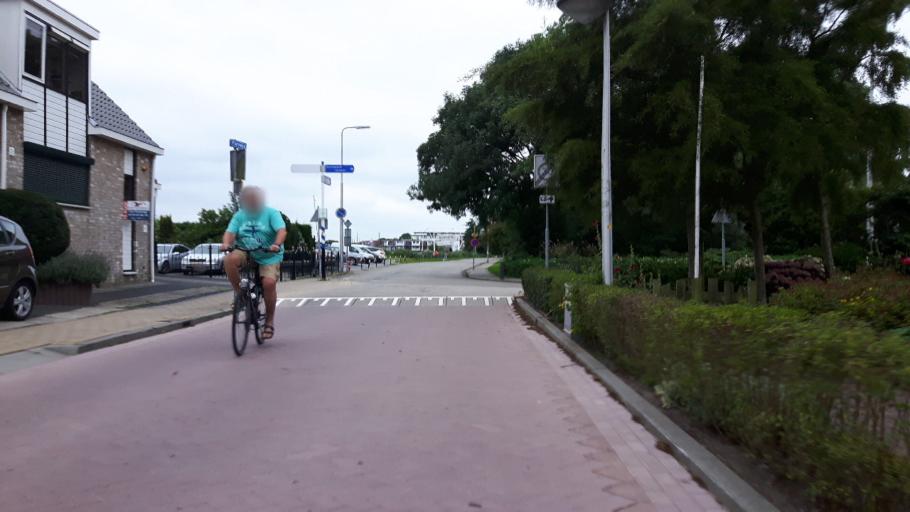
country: NL
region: South Holland
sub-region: Gemeente Kaag en Braassem
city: Oude Wetering
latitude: 52.2055
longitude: 4.6463
